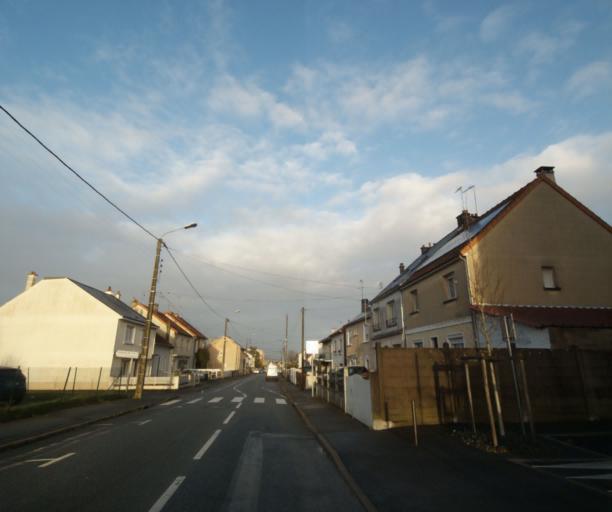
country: FR
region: Pays de la Loire
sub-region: Departement de la Sarthe
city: Le Mans
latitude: 47.9780
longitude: 0.2199
